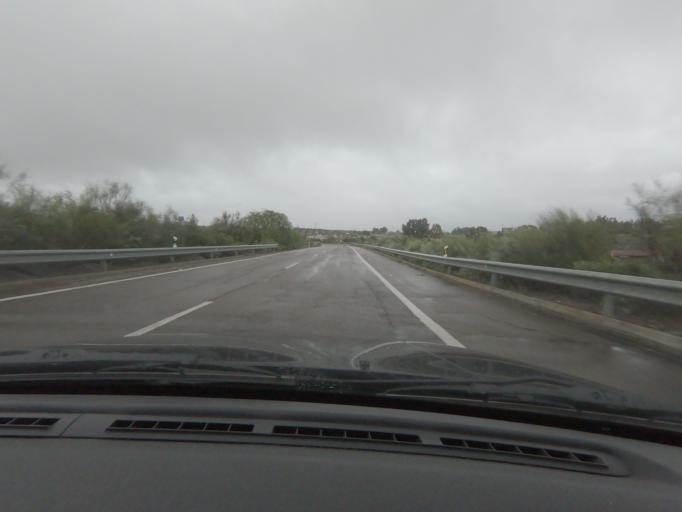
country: ES
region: Extremadura
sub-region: Provincia de Badajoz
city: Calamonte
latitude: 38.9065
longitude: -6.3767
